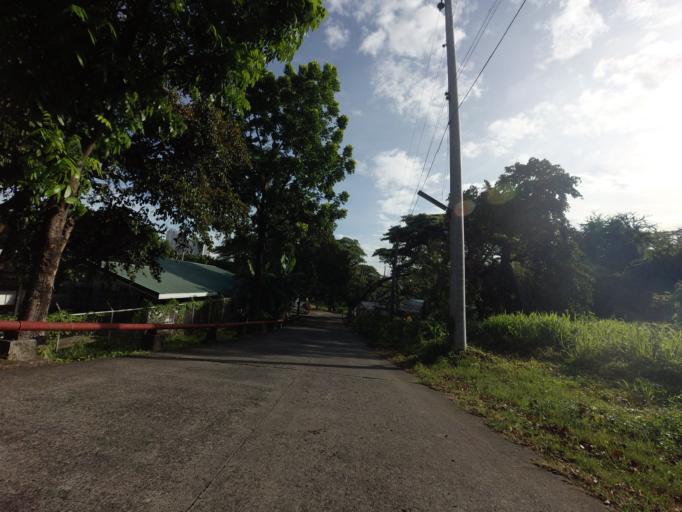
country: PH
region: Metro Manila
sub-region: Mandaluyong
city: Mandaluyong City
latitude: 14.5808
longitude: 121.0399
